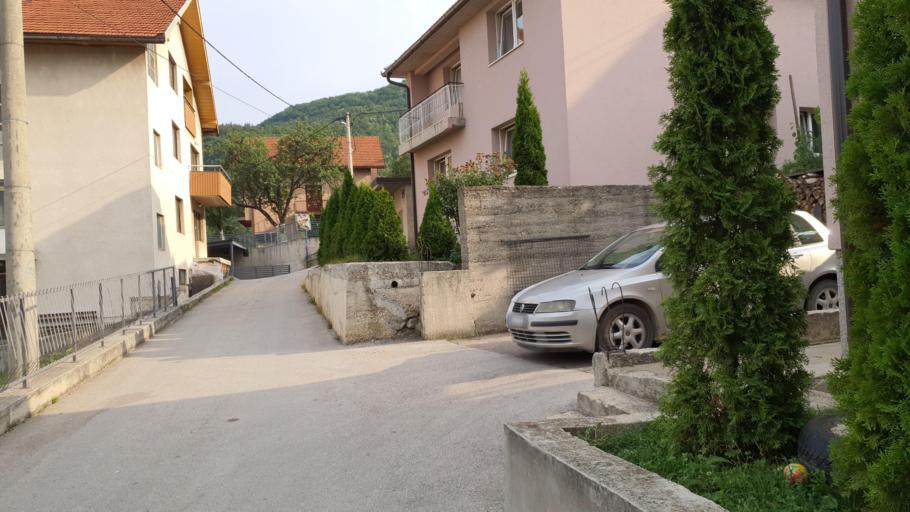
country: RS
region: Central Serbia
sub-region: Zlatiborski Okrug
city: Uzice
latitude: 43.8556
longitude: 19.8305
